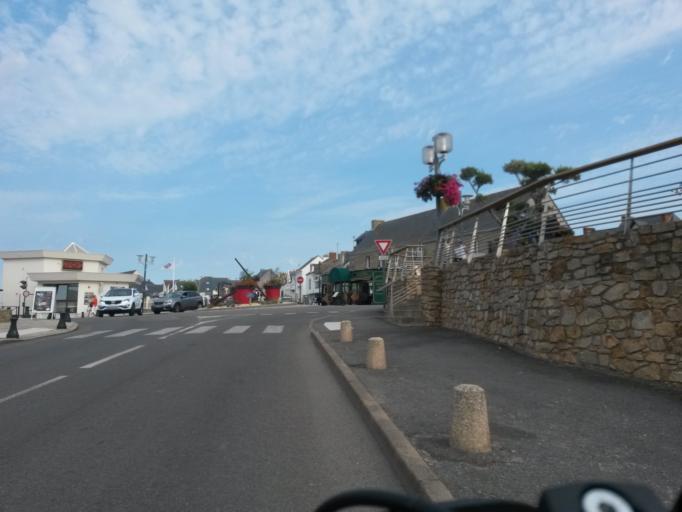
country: FR
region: Pays de la Loire
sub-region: Departement de la Loire-Atlantique
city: La Turballe
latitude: 47.3477
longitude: -2.5120
